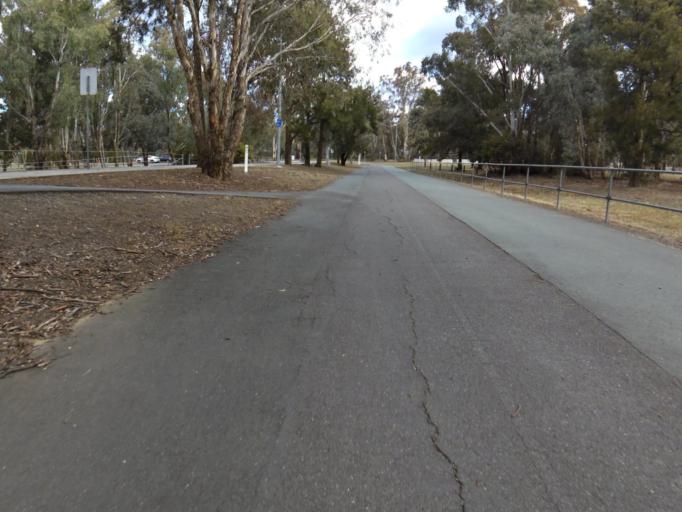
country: AU
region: Australian Capital Territory
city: Acton
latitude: -35.2497
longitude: 149.1049
